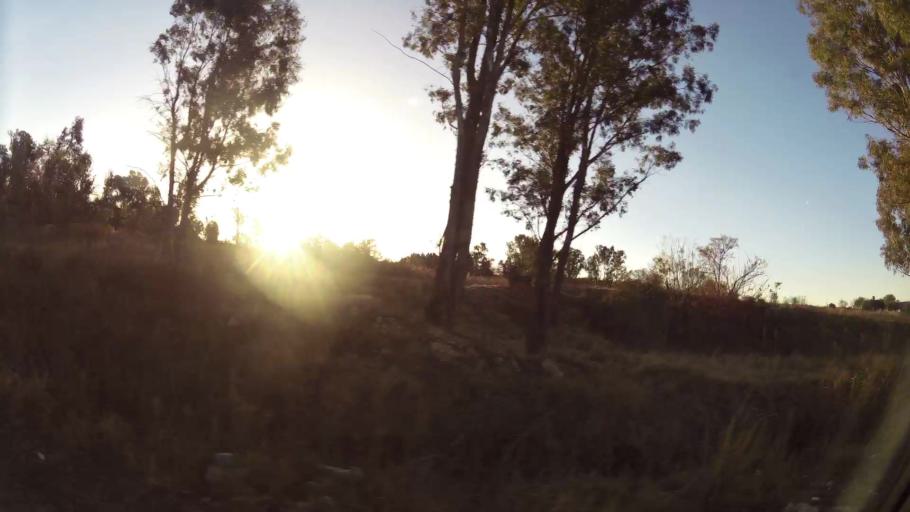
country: ZA
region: Gauteng
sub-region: City of Johannesburg Metropolitan Municipality
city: Diepsloot
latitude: -25.9494
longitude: 28.0222
